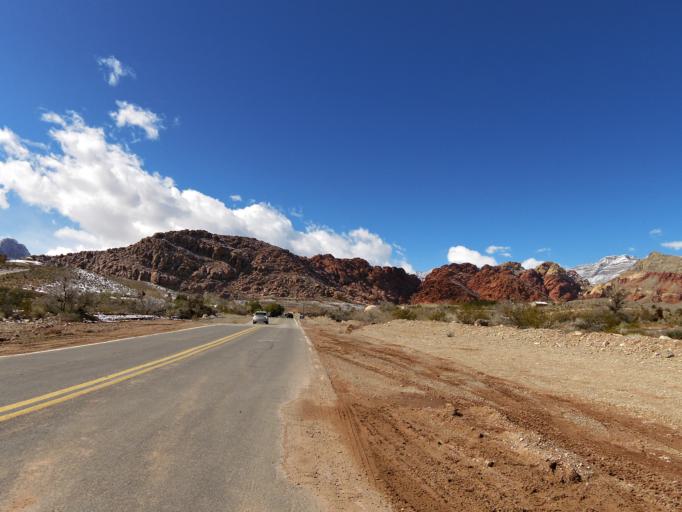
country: US
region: Nevada
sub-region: Clark County
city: Summerlin South
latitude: 36.1471
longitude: -115.4086
